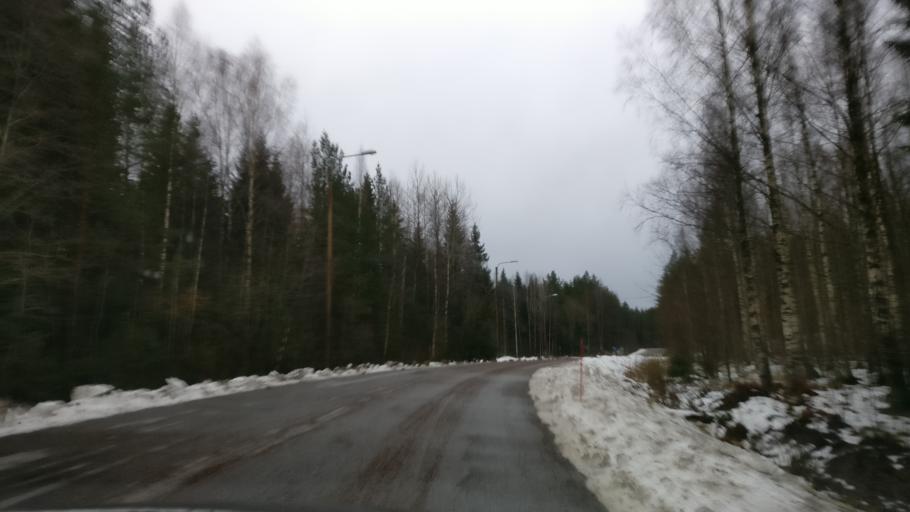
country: FI
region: Uusimaa
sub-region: Raaseporin
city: Karis
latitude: 60.0686
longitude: 23.8122
